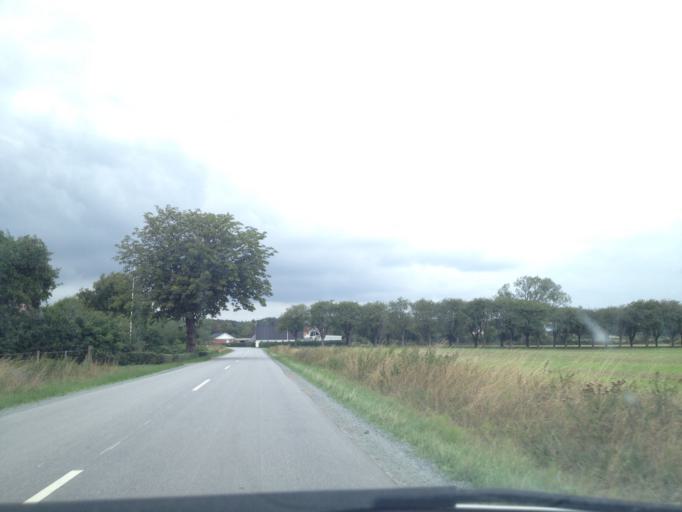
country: DK
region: South Denmark
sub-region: Haderslev Kommune
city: Starup
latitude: 55.3049
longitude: 9.5412
